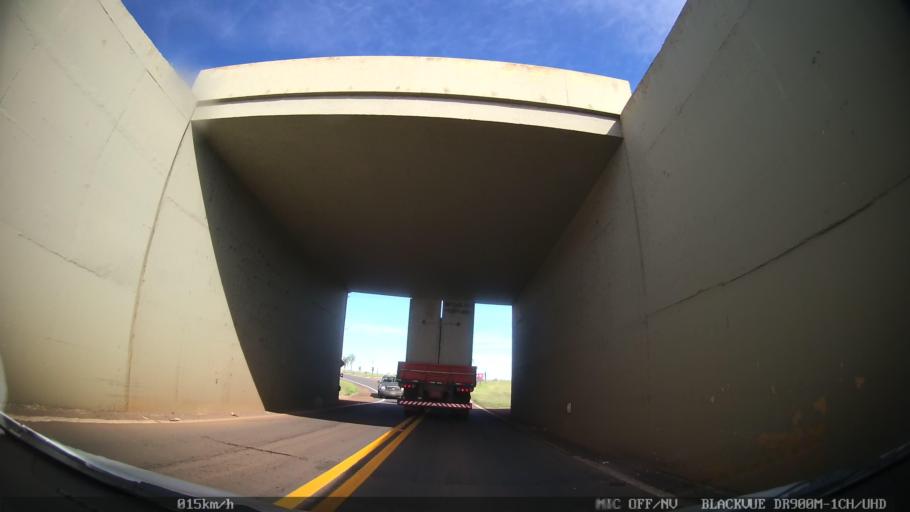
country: BR
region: Sao Paulo
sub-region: Araras
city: Araras
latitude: -22.3963
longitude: -47.3907
